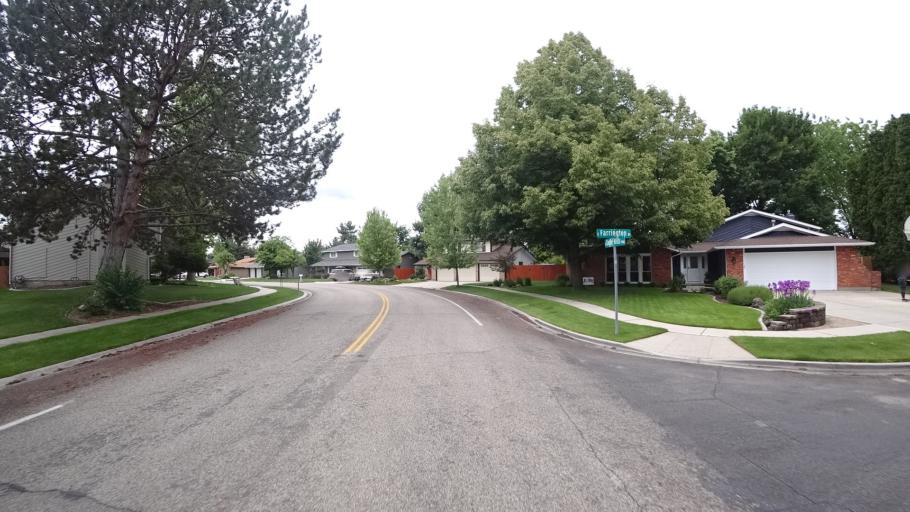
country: US
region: Idaho
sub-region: Ada County
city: Eagle
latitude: 43.7040
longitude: -116.3431
